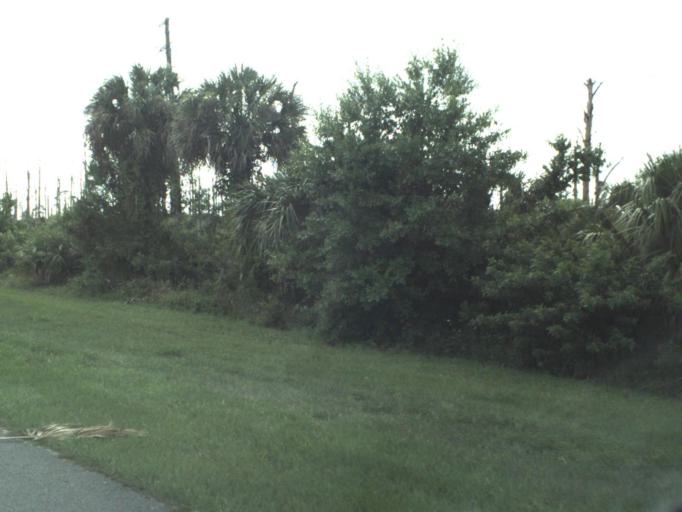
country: US
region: Florida
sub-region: Brevard County
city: Cocoa West
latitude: 28.3851
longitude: -80.7883
